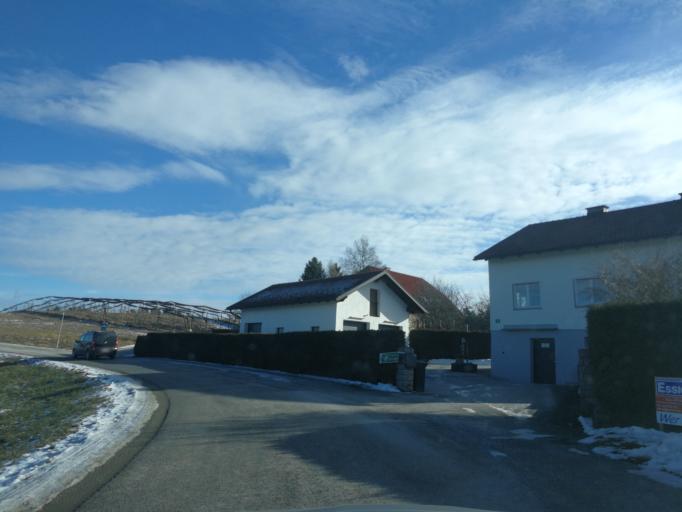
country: AT
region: Styria
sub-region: Politischer Bezirk Graz-Umgebung
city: Eggersdorf bei Graz
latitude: 47.1009
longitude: 15.6209
